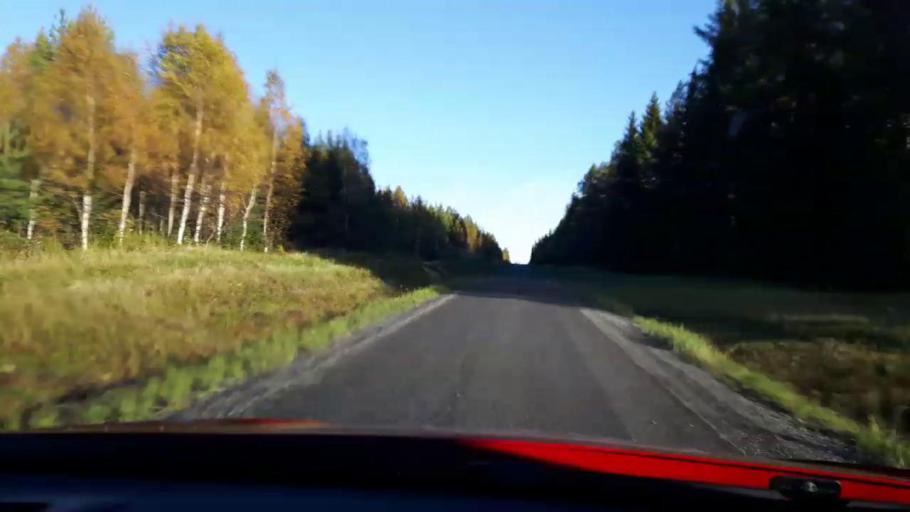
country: SE
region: Jaemtland
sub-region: OEstersunds Kommun
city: Lit
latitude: 63.5995
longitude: 14.8152
